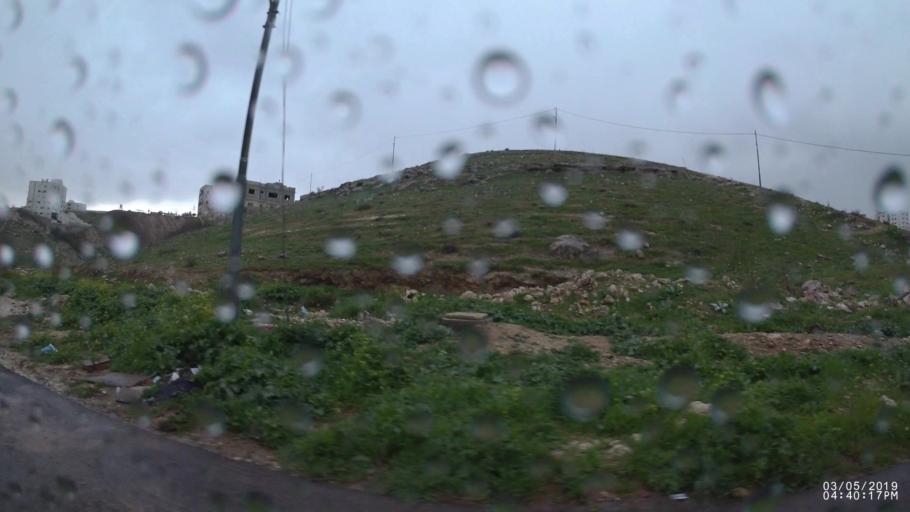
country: JO
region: Amman
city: Amman
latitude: 31.9975
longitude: 35.9660
